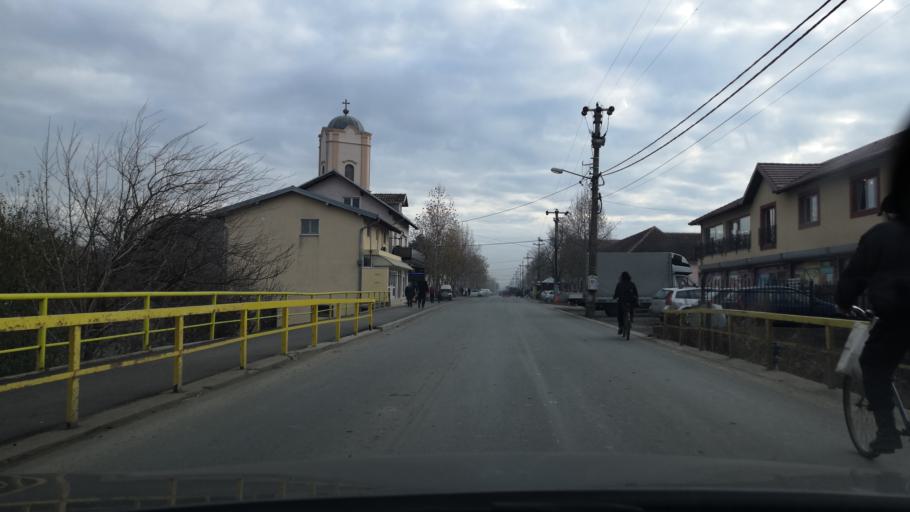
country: RS
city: Ugrinovci
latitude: 44.8761
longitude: 20.1859
